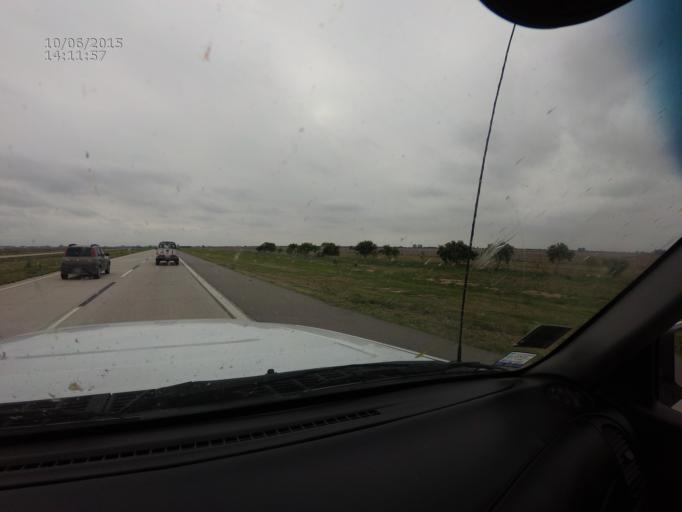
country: AR
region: Cordoba
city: Villa Maria
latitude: -32.4441
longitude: -63.1118
